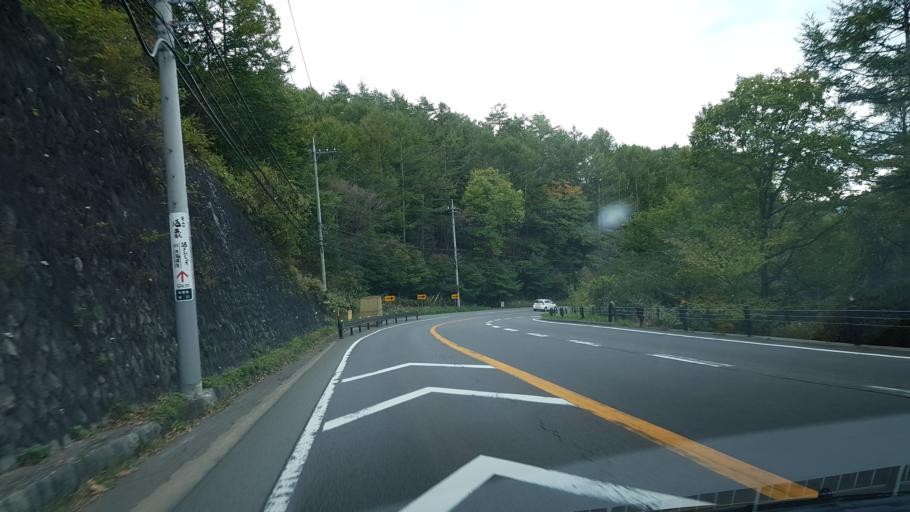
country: JP
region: Gunma
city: Nakanojomachi
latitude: 36.6007
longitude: 138.5868
